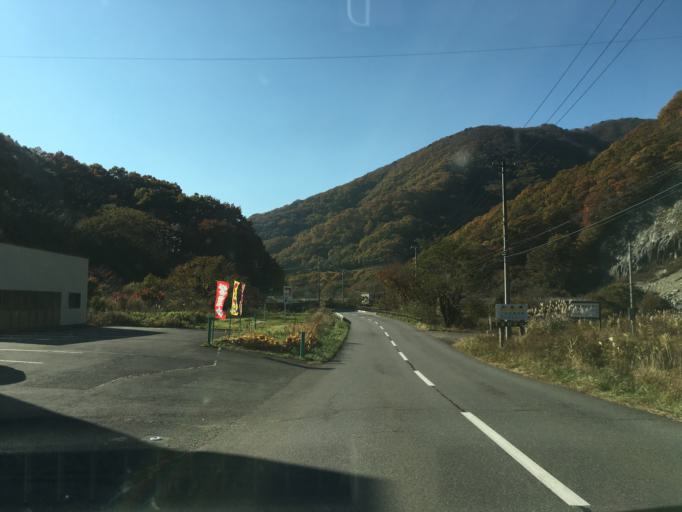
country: JP
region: Fukushima
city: Inawashiro
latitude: 37.2763
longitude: 140.0485
